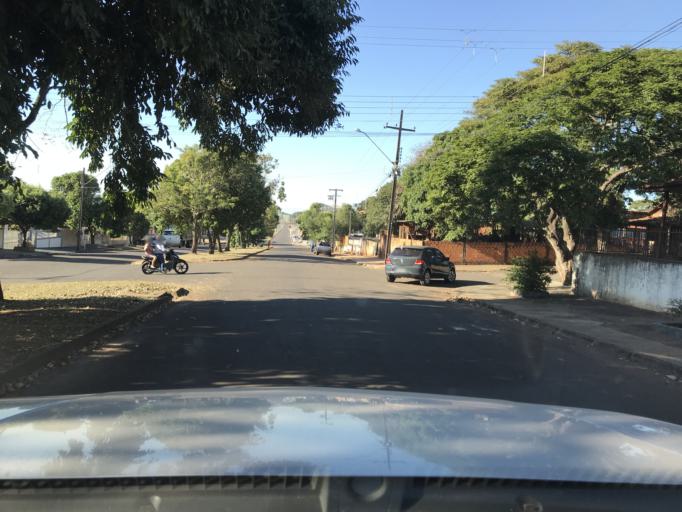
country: BR
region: Parana
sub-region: Ipora
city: Ipora
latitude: -23.9978
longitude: -53.7048
